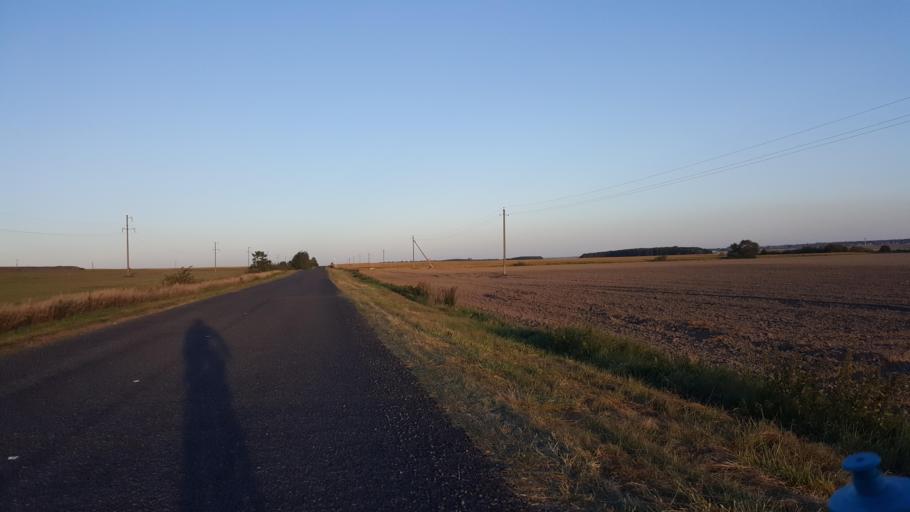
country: BY
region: Brest
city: Vysokaye
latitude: 52.2937
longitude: 23.5461
